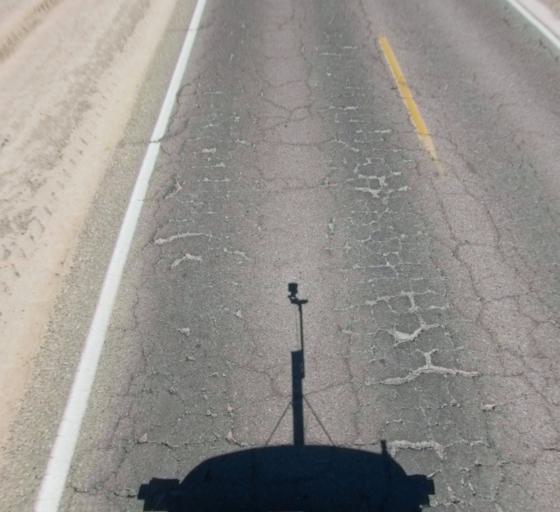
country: US
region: California
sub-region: Fresno County
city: Mendota
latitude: 36.8567
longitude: -120.3338
